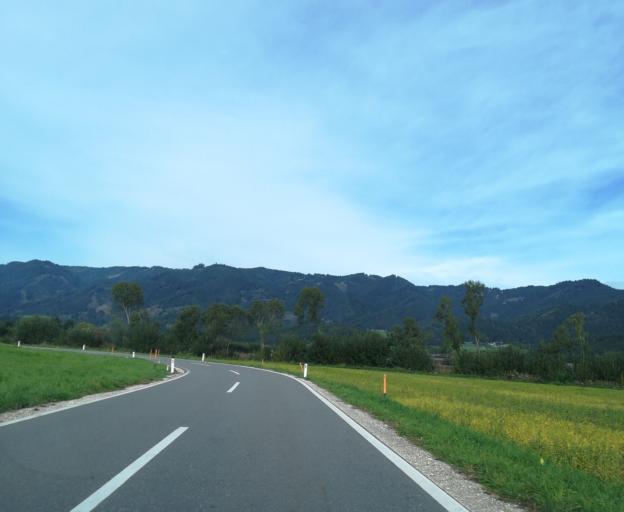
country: AT
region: Styria
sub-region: Politischer Bezirk Murtal
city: Flatschach
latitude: 47.2065
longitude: 14.7593
